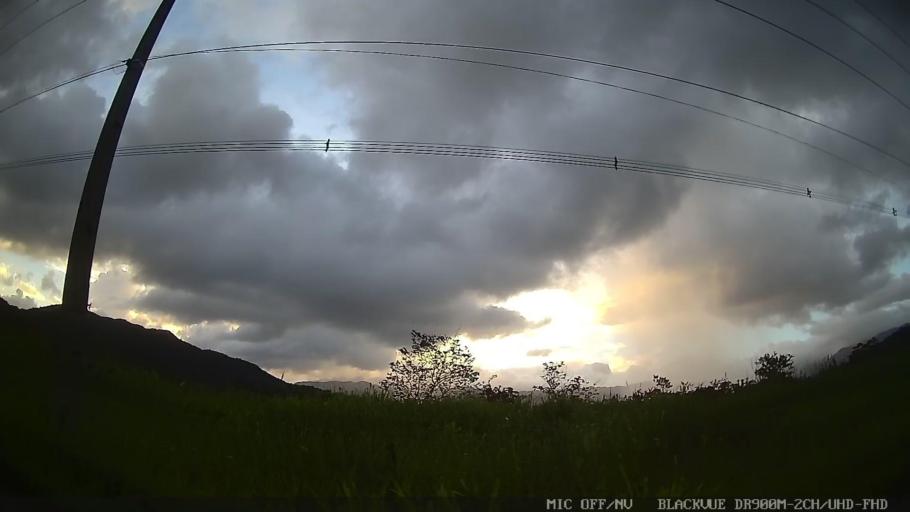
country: BR
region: Sao Paulo
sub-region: Itanhaem
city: Itanhaem
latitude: -24.0951
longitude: -46.7995
